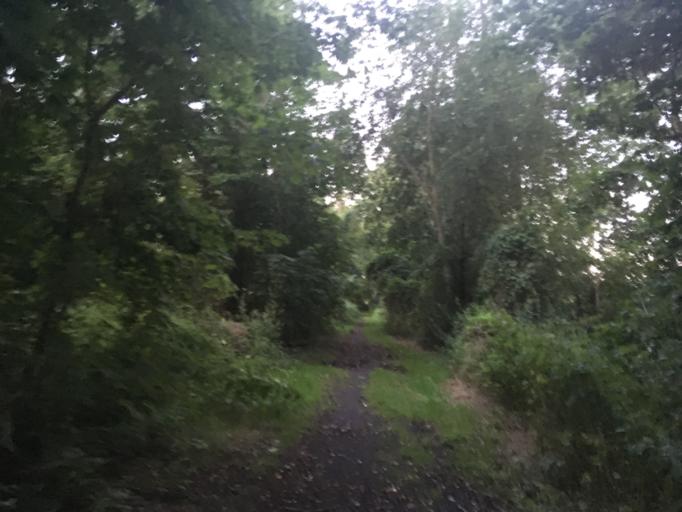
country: DE
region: Brandenburg
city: Erkner
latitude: 52.4143
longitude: 13.7437
